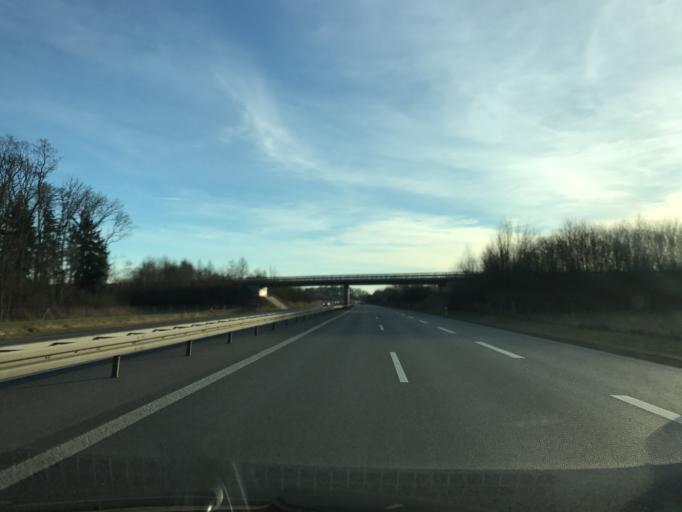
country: DE
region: Baden-Wuerttemberg
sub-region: Tuebingen Region
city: Baindt
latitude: 47.8498
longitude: 9.6394
